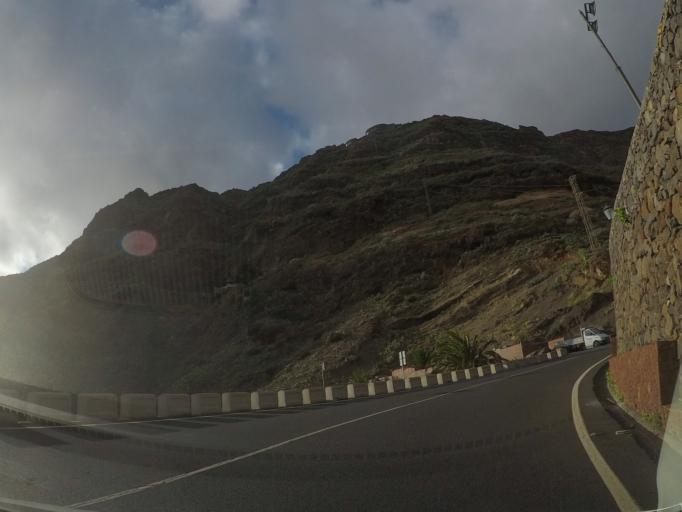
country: ES
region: Canary Islands
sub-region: Provincia de Santa Cruz de Tenerife
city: Vallehermosa
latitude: 28.1176
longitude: -17.3130
